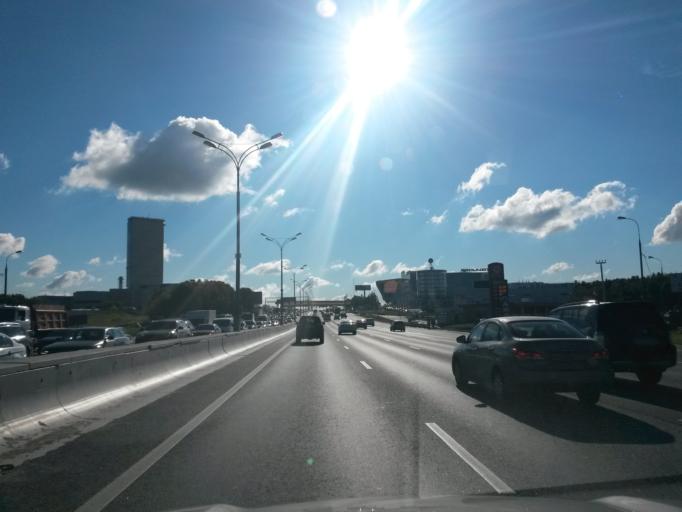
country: RU
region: Moscow
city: Annino
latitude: 55.5757
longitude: 37.6022
